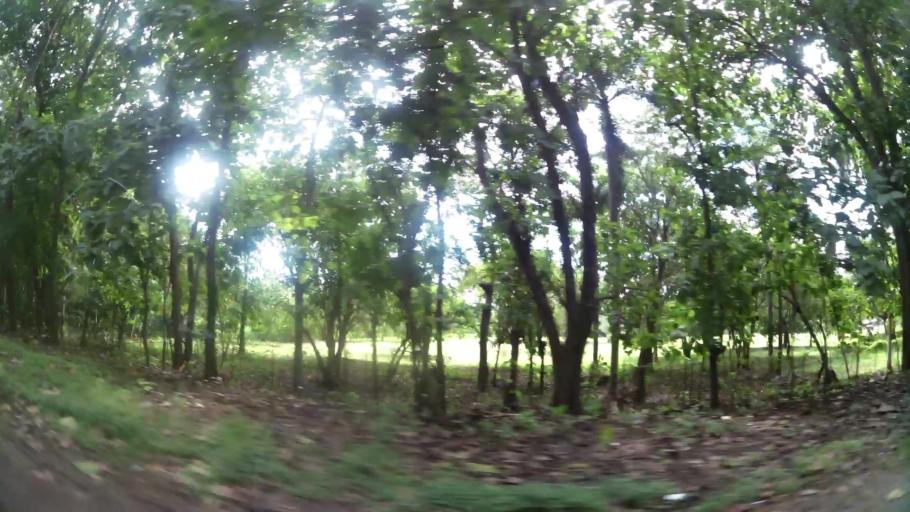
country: PA
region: Panama
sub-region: Distrito de Panama
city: Paraiso
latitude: 9.0142
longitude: -79.5999
